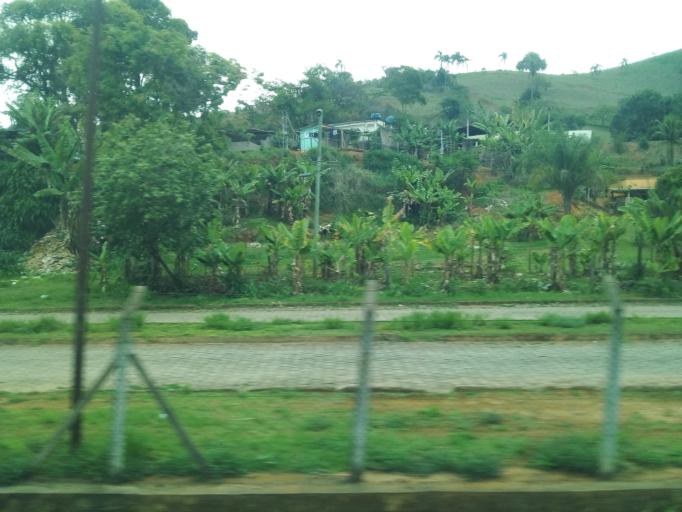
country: BR
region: Minas Gerais
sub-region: Nova Era
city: Nova Era
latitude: -19.7401
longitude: -43.0180
